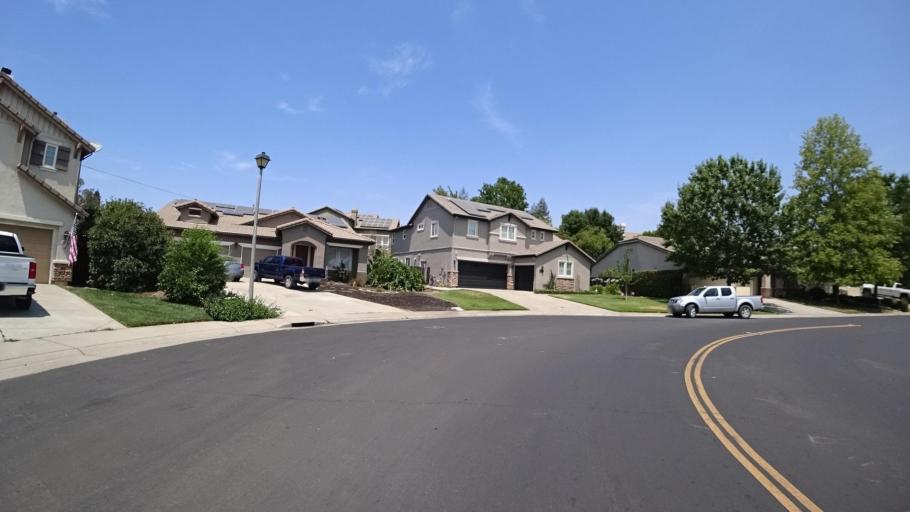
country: US
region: California
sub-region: Placer County
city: Rocklin
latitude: 38.8031
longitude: -121.2283
